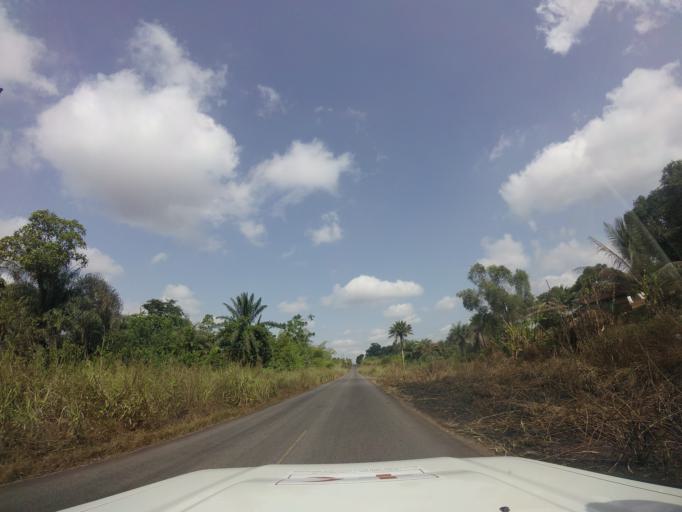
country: LR
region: Bomi
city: Tubmanburg
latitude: 6.7065
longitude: -10.9258
